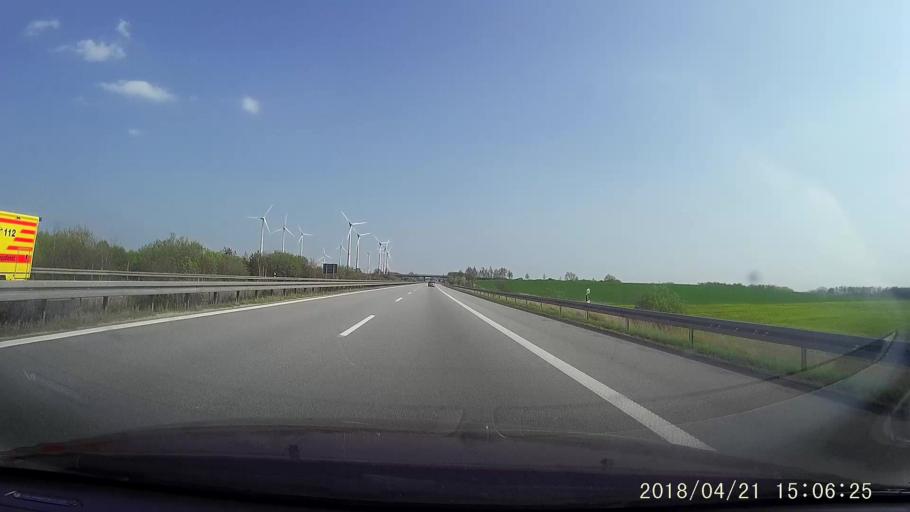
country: DE
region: Saxony
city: Kodersdorf
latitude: 51.2142
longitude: 14.9347
